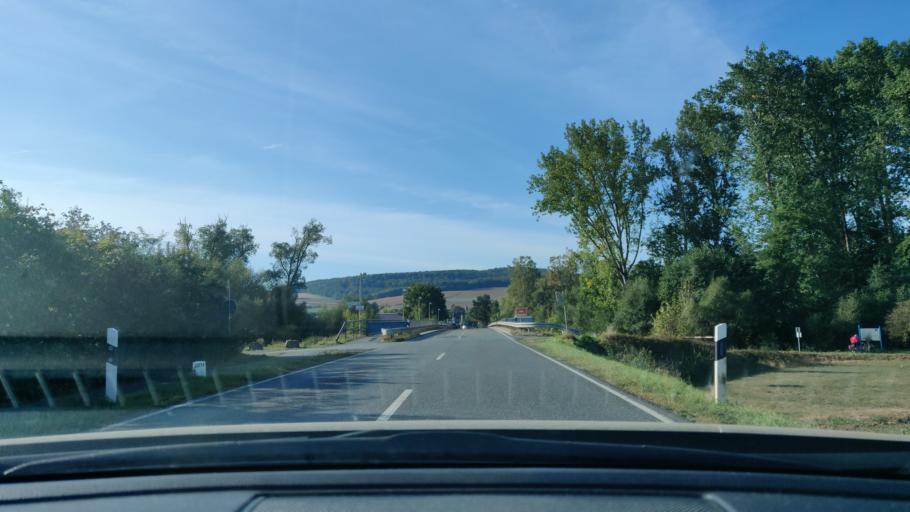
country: DE
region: Hesse
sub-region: Regierungsbezirk Kassel
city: Bad Wildungen
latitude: 51.1377
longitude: 9.1770
